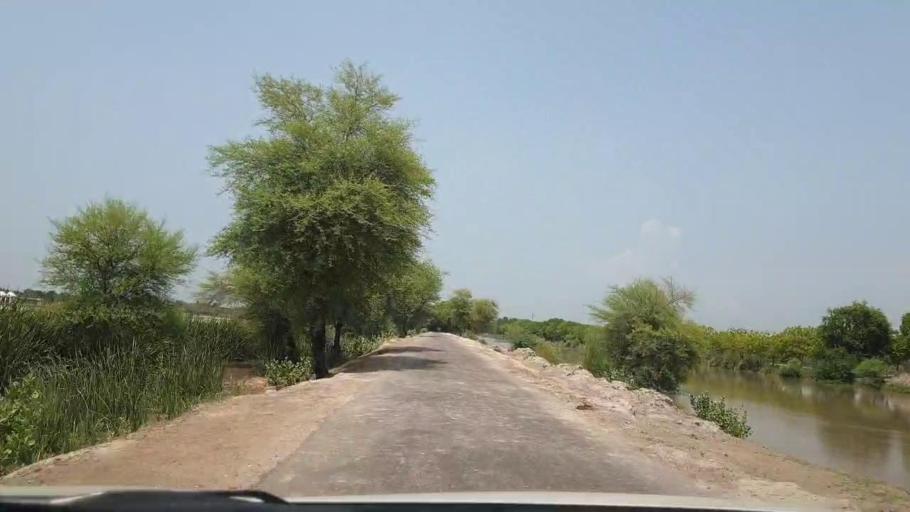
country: PK
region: Sindh
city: Dokri
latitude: 27.3563
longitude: 68.1131
